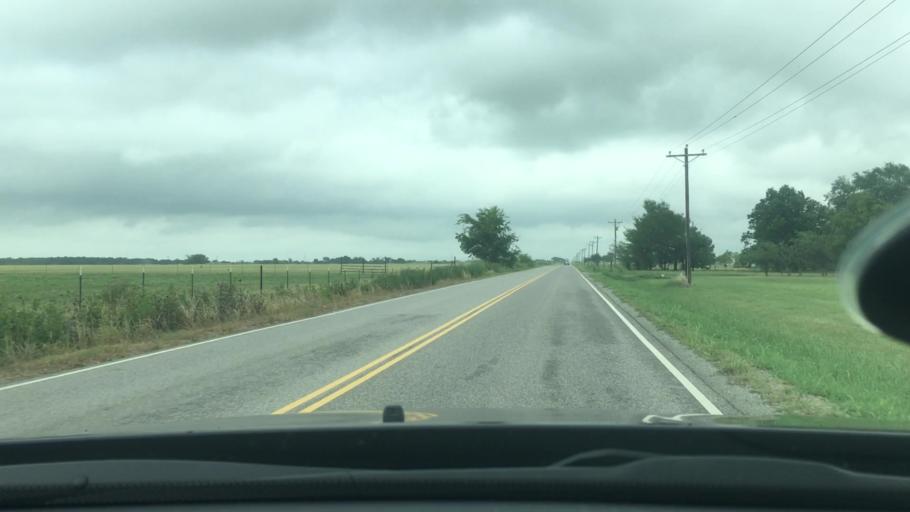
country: US
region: Oklahoma
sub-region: Bryan County
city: Colbert
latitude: 33.9029
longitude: -96.5006
